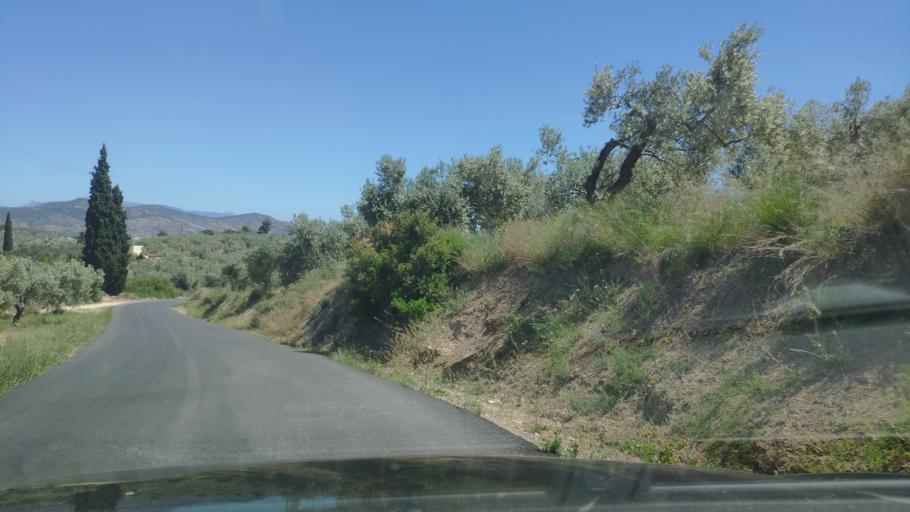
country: GR
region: Peloponnese
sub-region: Nomos Korinthias
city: Athikia
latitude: 37.8044
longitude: 22.9039
